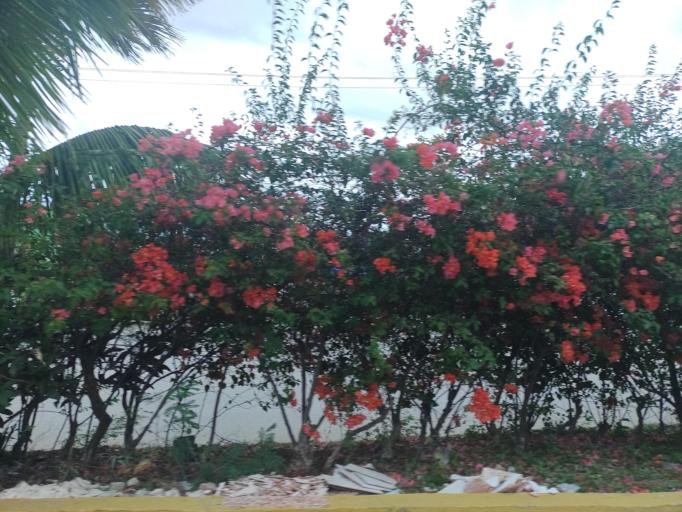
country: MX
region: Quintana Roo
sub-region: Tulum
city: Ciudad Chemuyil
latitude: 20.4003
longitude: -87.3208
